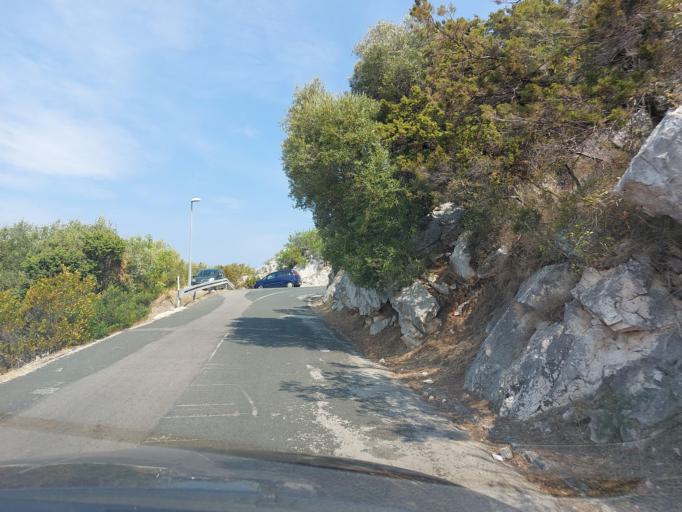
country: HR
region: Dubrovacko-Neretvanska
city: Smokvica
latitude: 42.7729
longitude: 16.8782
